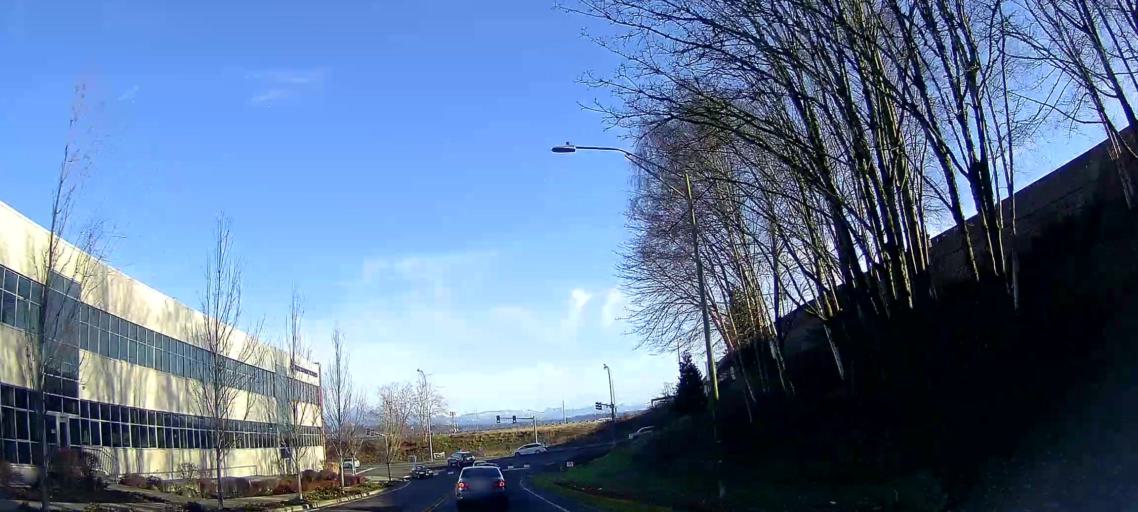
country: US
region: Washington
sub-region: Snohomish County
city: Everett
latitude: 47.9647
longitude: -122.2023
